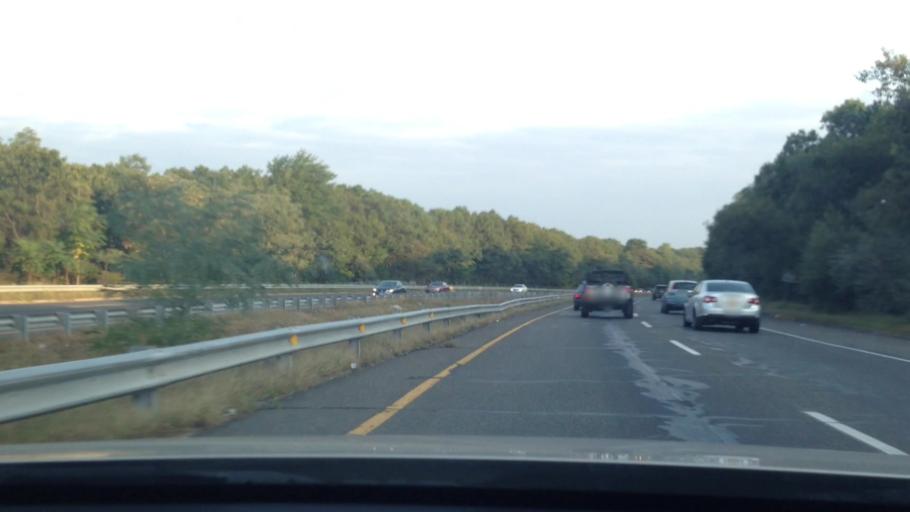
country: US
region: New York
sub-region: Suffolk County
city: Selden
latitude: 40.8547
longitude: -73.0204
